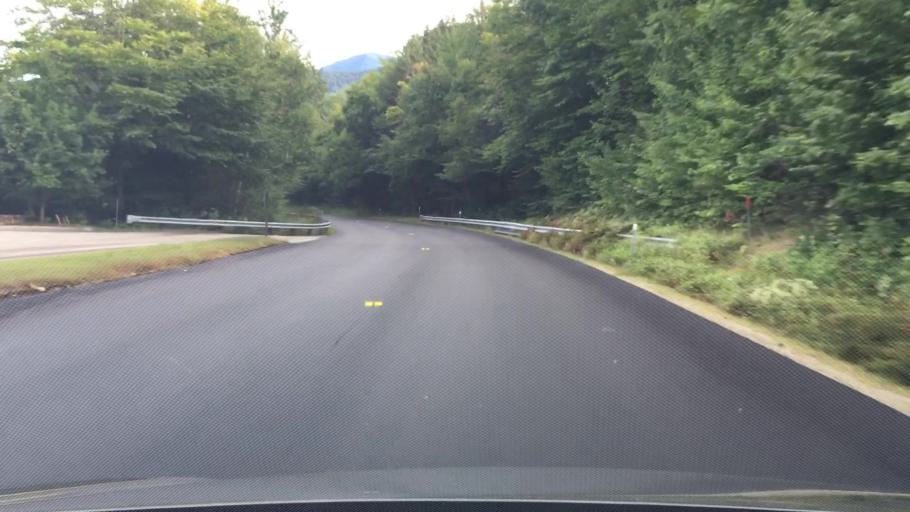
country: US
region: New Hampshire
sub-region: Carroll County
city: Sandwich
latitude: 44.0095
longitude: -71.4279
